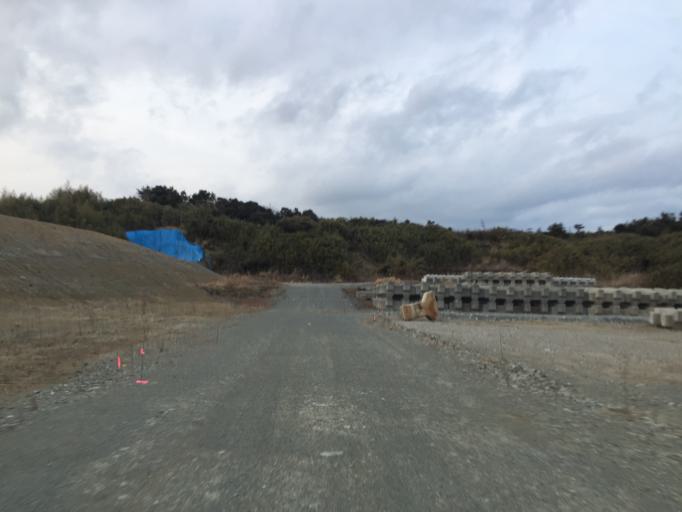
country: JP
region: Fukushima
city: Namie
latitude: 37.7612
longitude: 140.9991
